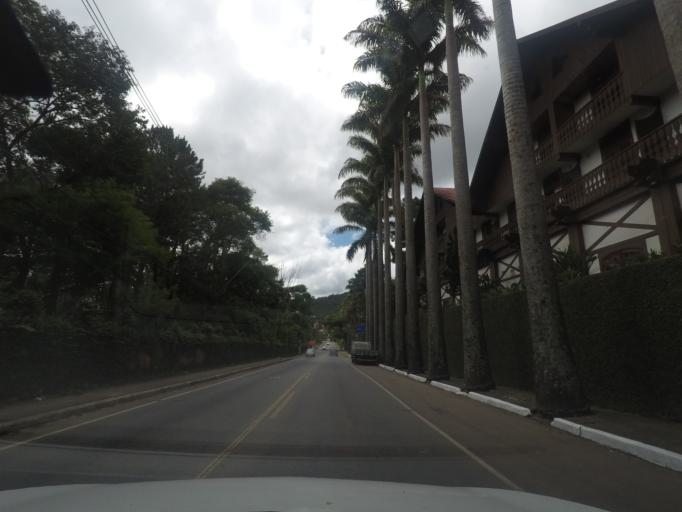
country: BR
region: Rio de Janeiro
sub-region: Teresopolis
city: Teresopolis
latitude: -22.3938
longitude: -42.9869
